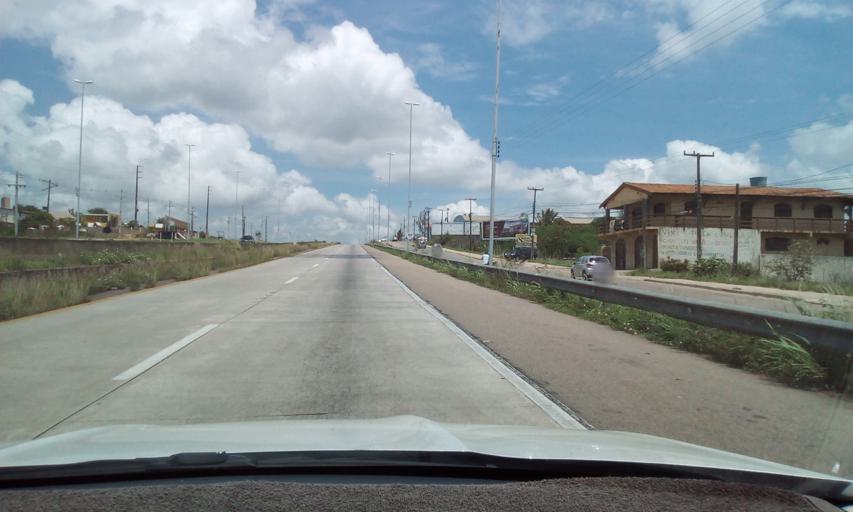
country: BR
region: Pernambuco
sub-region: Gravata
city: Gravata
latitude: -8.1971
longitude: -35.5797
